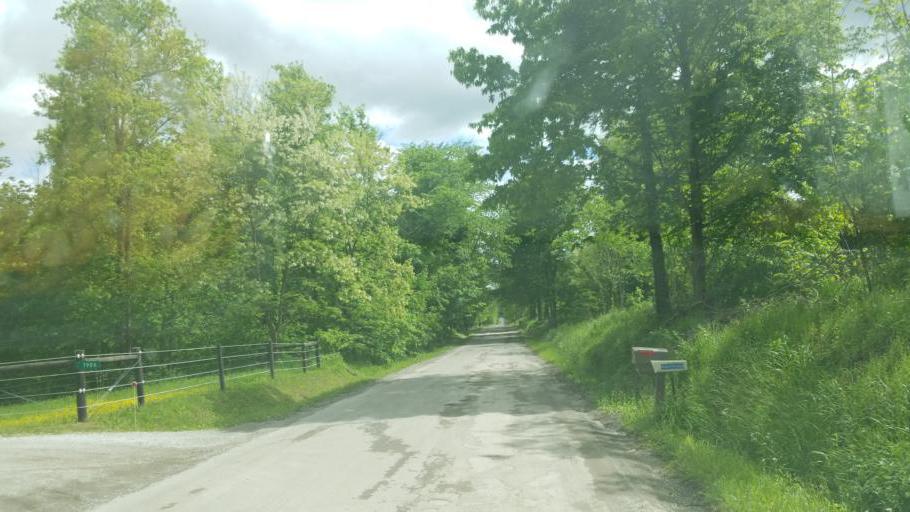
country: US
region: Ohio
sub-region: Geauga County
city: Middlefield
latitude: 41.4364
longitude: -81.0033
